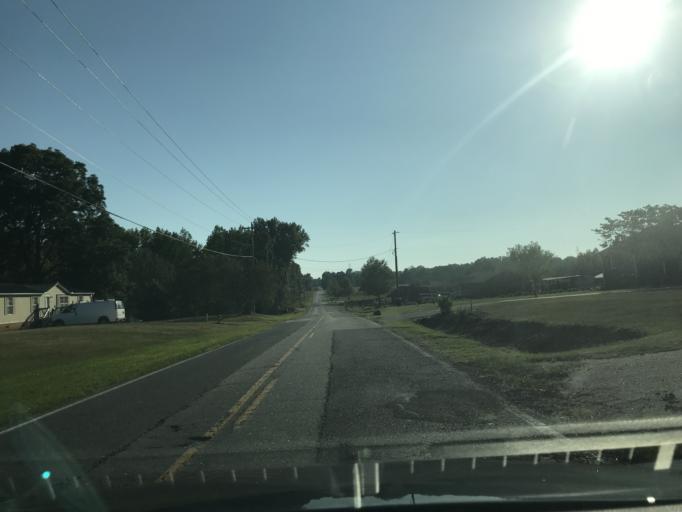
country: US
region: South Carolina
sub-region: Spartanburg County
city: Mayo
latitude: 35.1400
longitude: -81.7559
